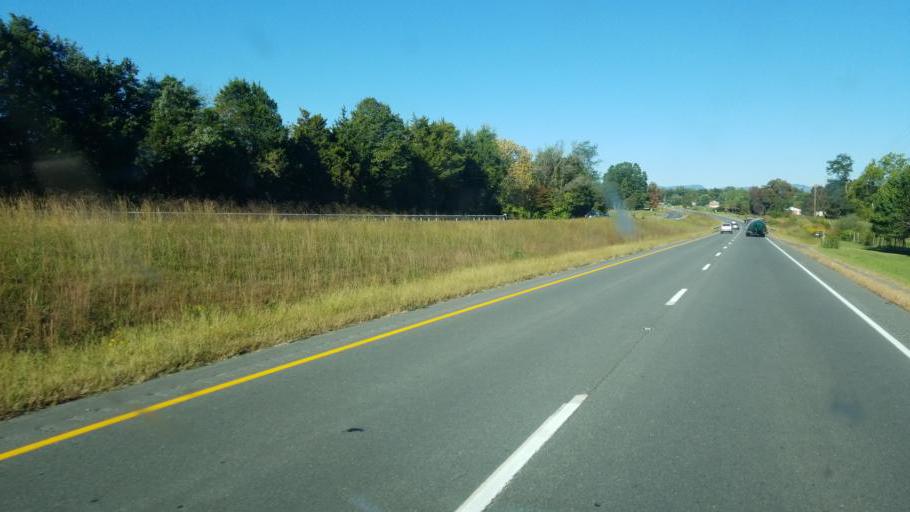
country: US
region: Virginia
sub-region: Culpeper County
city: Merrimac
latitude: 38.4531
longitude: -78.1046
